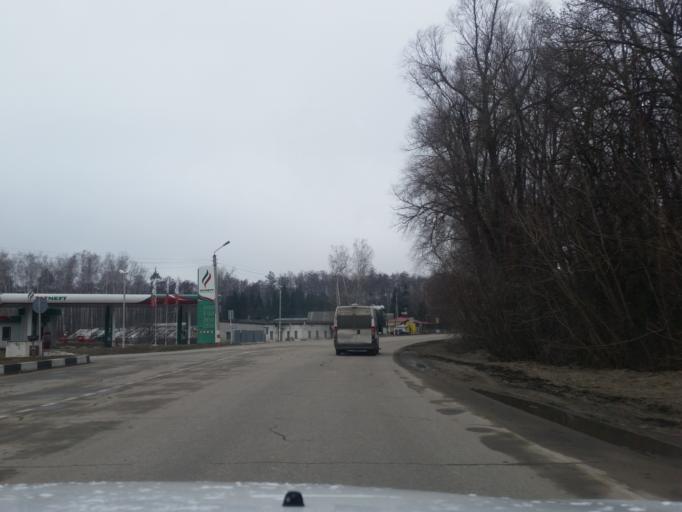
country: RU
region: Ulyanovsk
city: Dimitrovgrad
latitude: 54.2130
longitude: 49.5418
